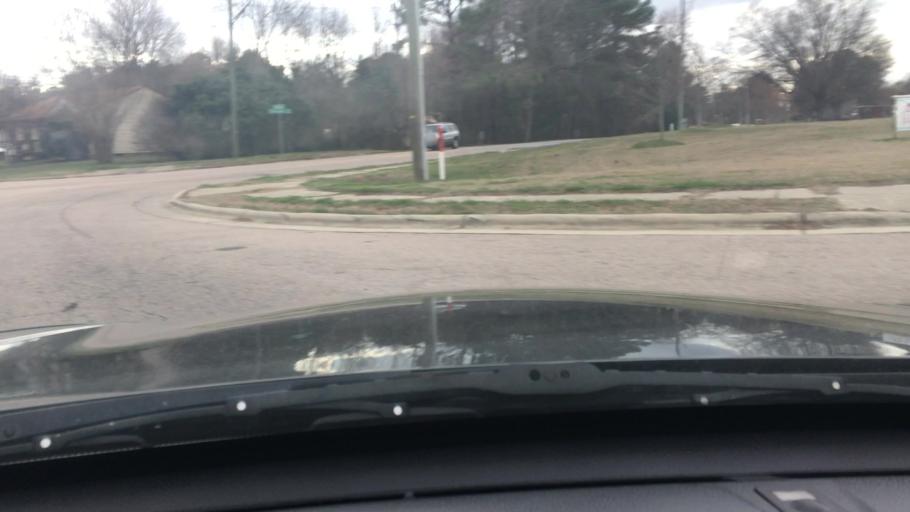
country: US
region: North Carolina
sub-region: Wake County
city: Raleigh
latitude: 35.8306
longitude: -78.5781
